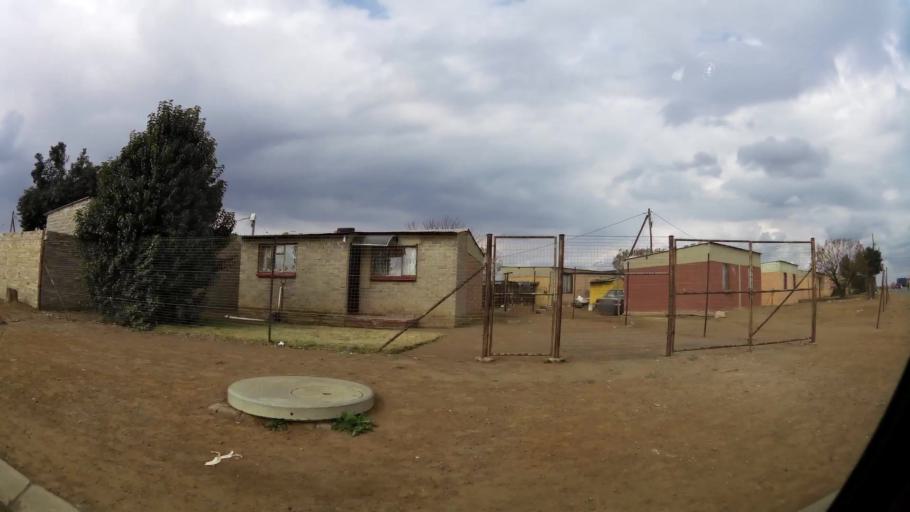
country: ZA
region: Gauteng
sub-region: Sedibeng District Municipality
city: Vanderbijlpark
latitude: -26.6851
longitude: 27.7796
